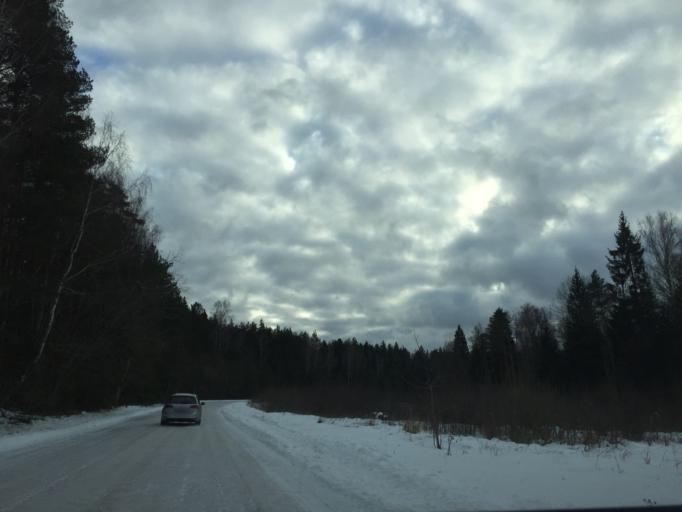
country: LV
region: Lielvarde
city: Lielvarde
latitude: 56.6238
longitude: 24.7732
